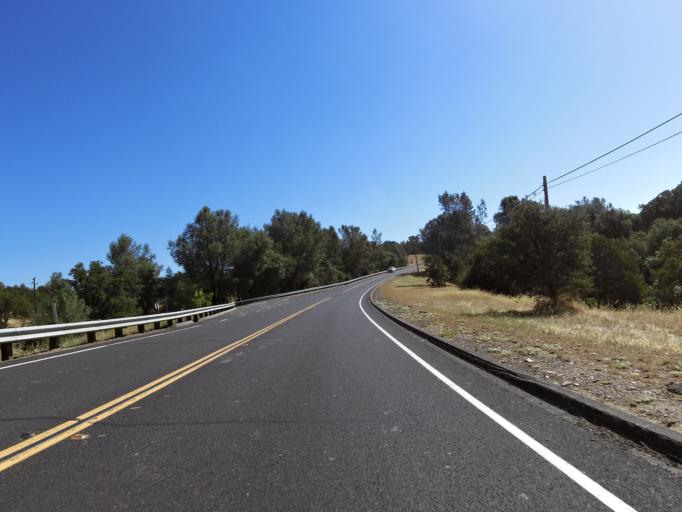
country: US
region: California
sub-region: Tuolumne County
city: Jamestown
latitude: 37.7101
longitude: -120.3326
